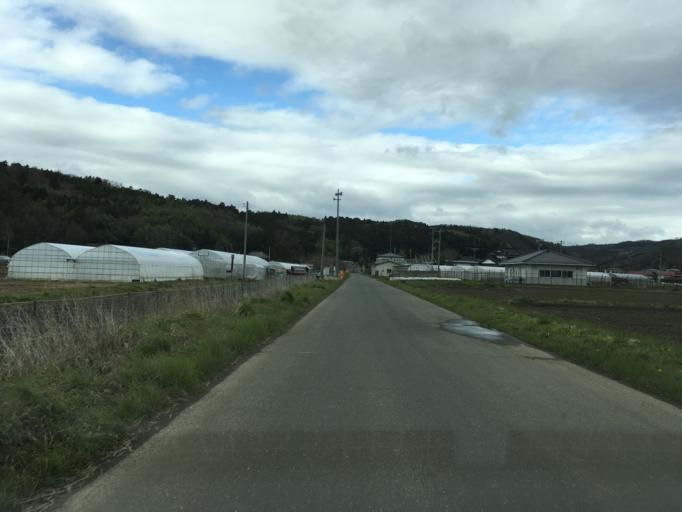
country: JP
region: Iwate
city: Ichinoseki
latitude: 38.7594
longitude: 141.2667
